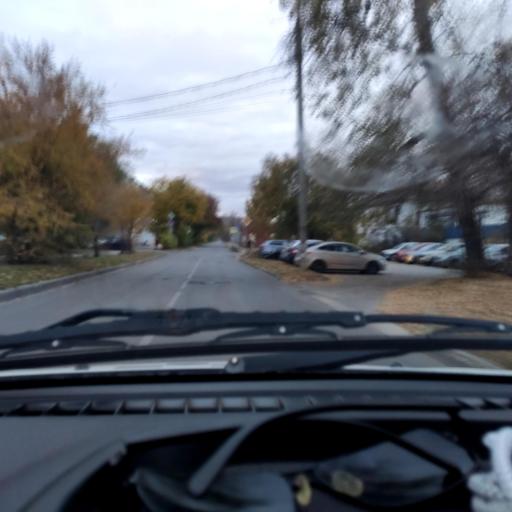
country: RU
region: Samara
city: Zhigulevsk
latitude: 53.4696
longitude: 49.5306
